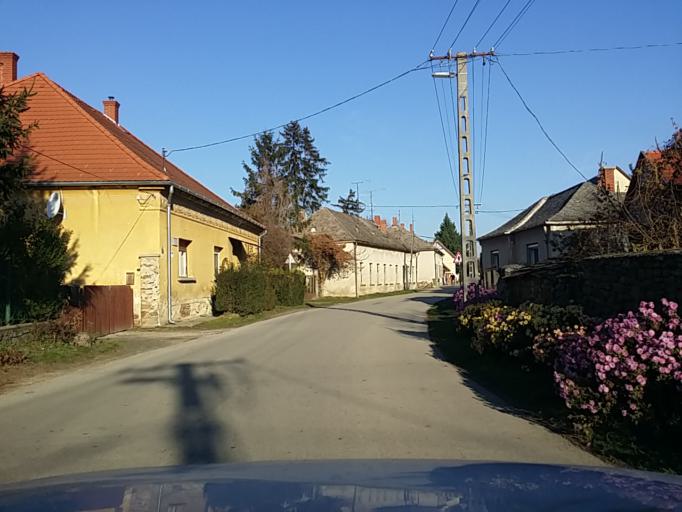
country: HU
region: Veszprem
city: Badacsonytomaj
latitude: 46.8482
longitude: 17.5134
